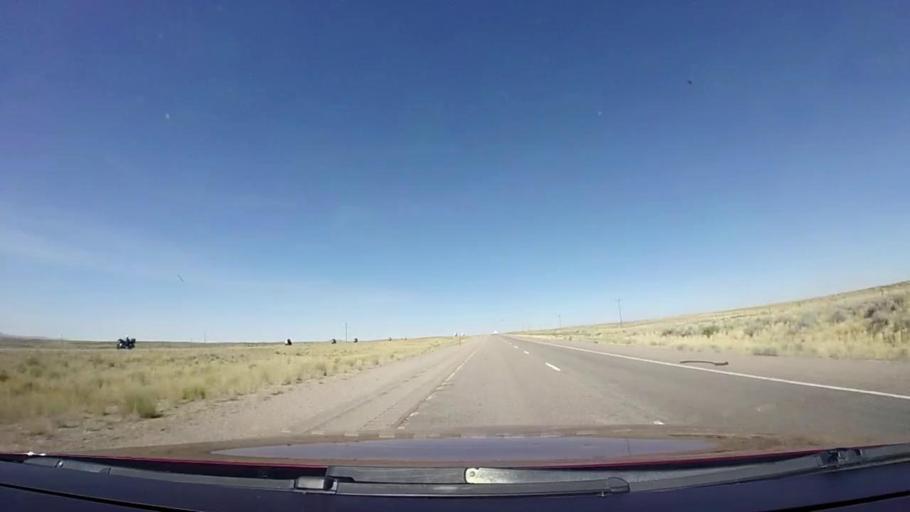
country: US
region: Wyoming
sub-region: Sweetwater County
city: Rock Springs
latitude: 41.6379
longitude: -108.4483
